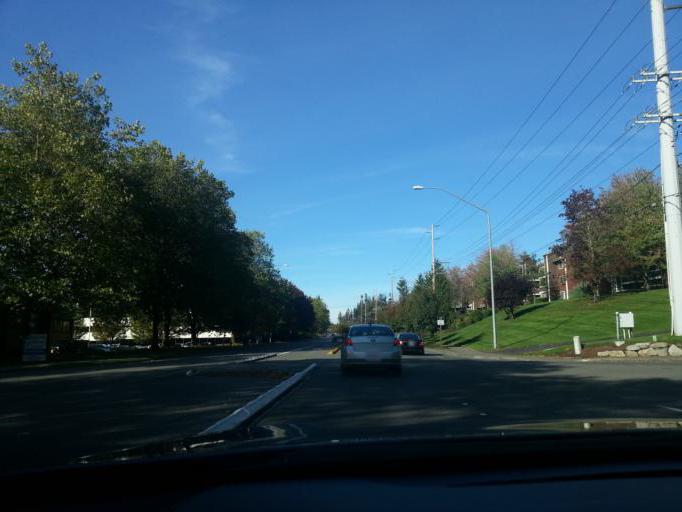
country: US
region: Washington
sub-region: Snohomish County
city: Mill Creek
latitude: 47.8519
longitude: -122.2181
